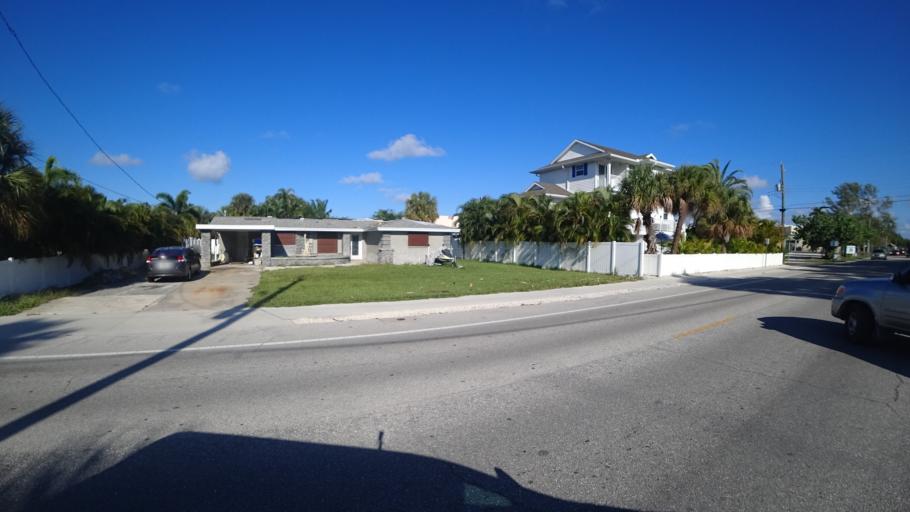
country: US
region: Florida
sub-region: Manatee County
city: Anna Maria
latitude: 27.5222
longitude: -82.7296
